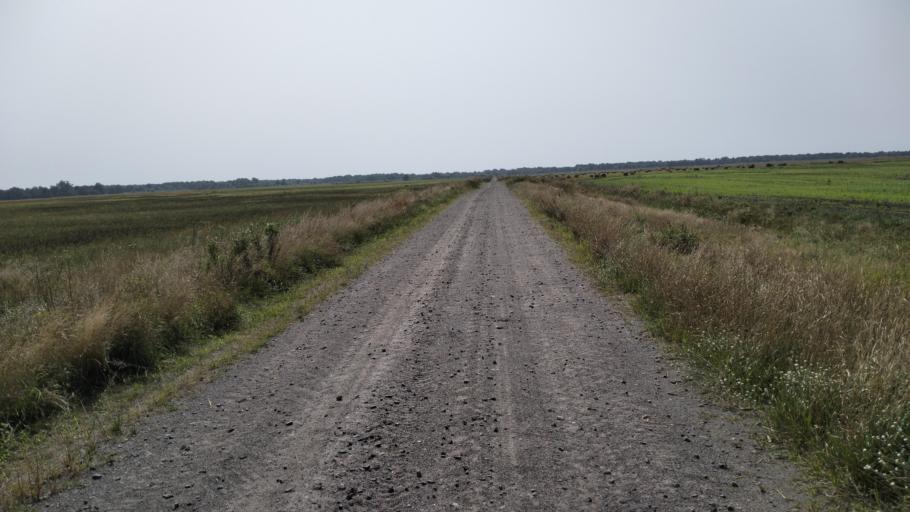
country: BY
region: Brest
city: Davyd-Haradok
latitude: 51.9837
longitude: 27.1752
